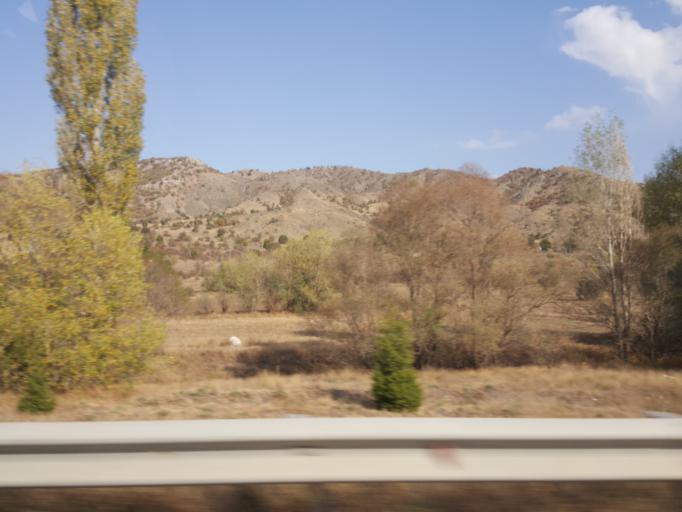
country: TR
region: Corum
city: Seydim
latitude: 40.3708
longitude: 34.7287
